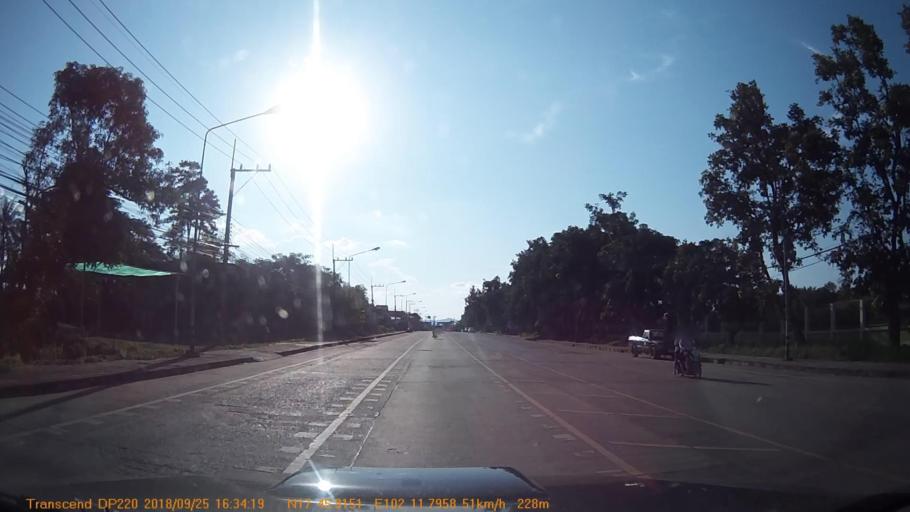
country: TH
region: Changwat Udon Thani
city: Nam Som
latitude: 17.7652
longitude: 102.1966
